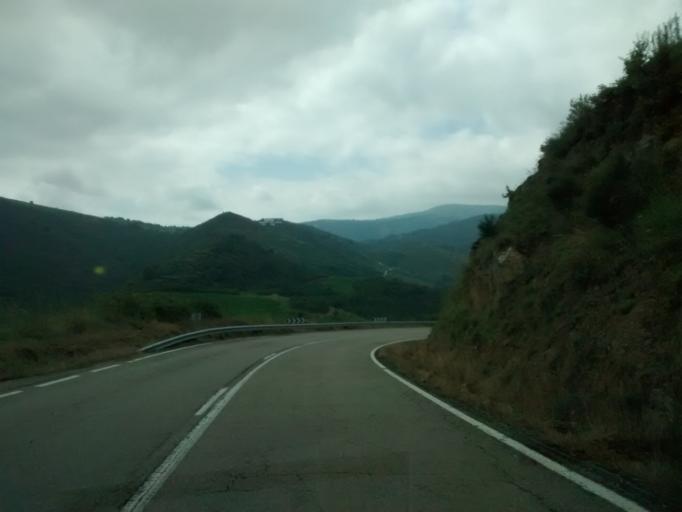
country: ES
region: Galicia
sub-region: Provincia de Ourense
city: Manzaneda
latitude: 42.3230
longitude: -7.2136
